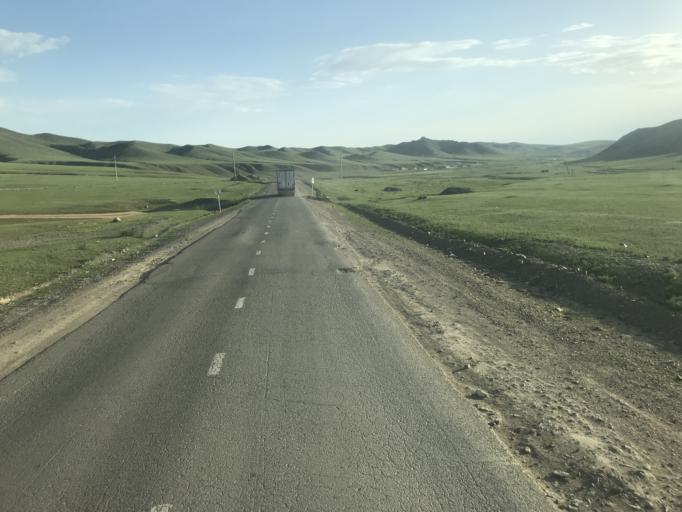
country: MN
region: Central Aimak
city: Bornuur
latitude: 48.4298
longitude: 106.1930
